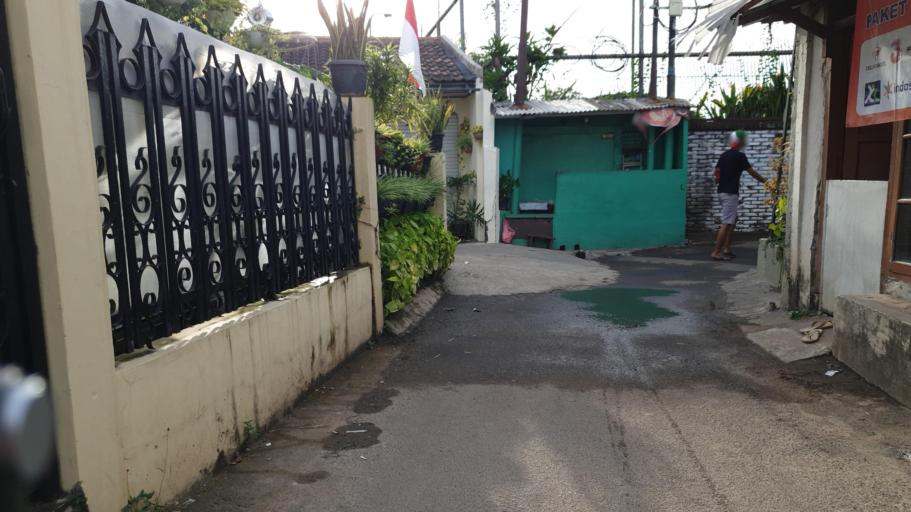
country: ID
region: Banten
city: South Tangerang
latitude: -6.2885
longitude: 106.7893
